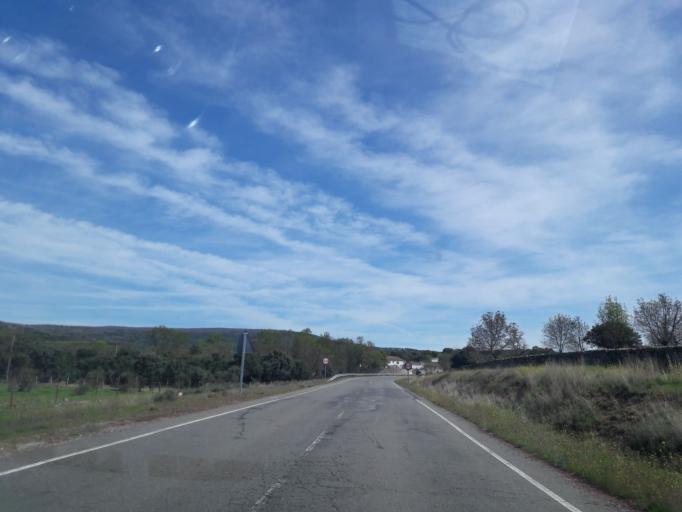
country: ES
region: Castille and Leon
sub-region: Provincia de Salamanca
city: Ledrada
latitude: 40.4882
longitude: -5.7222
